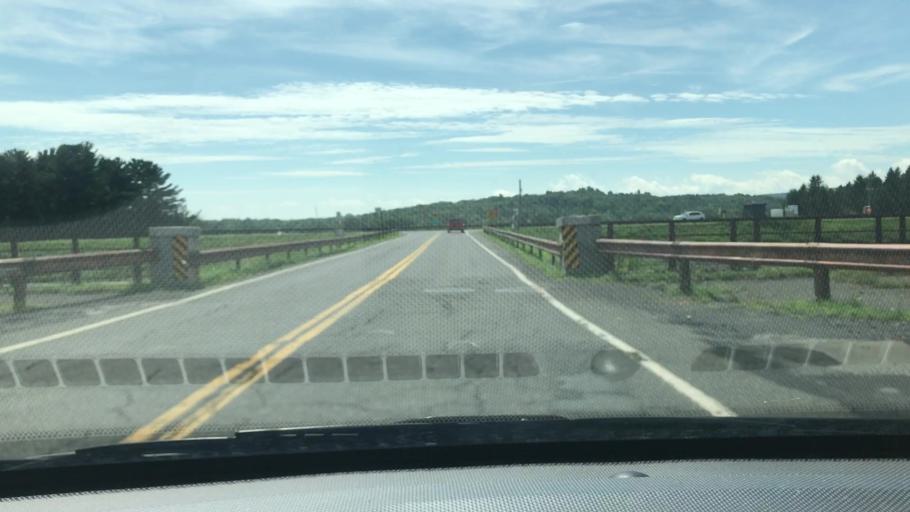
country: US
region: New York
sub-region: Ulster County
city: Shokan
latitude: 41.9503
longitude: -74.2078
